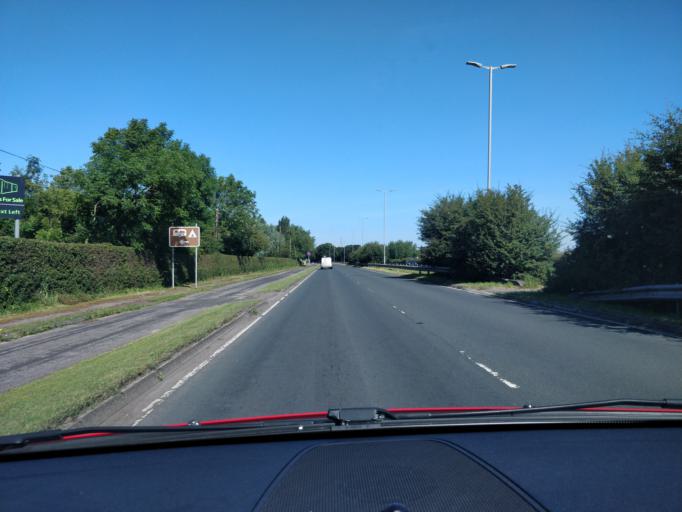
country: GB
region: England
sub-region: Lancashire
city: Banks
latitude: 53.6659
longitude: -2.8976
